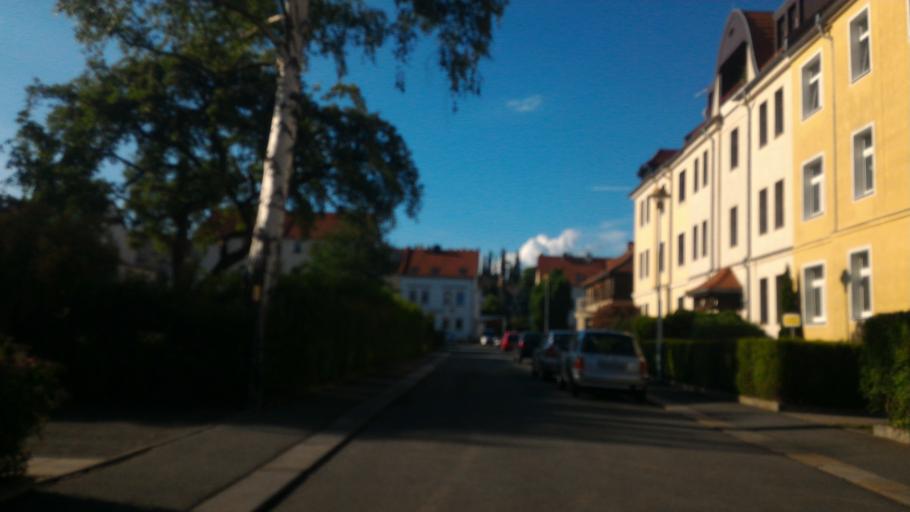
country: DE
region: Saxony
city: Zittau
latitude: 50.8970
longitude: 14.7898
